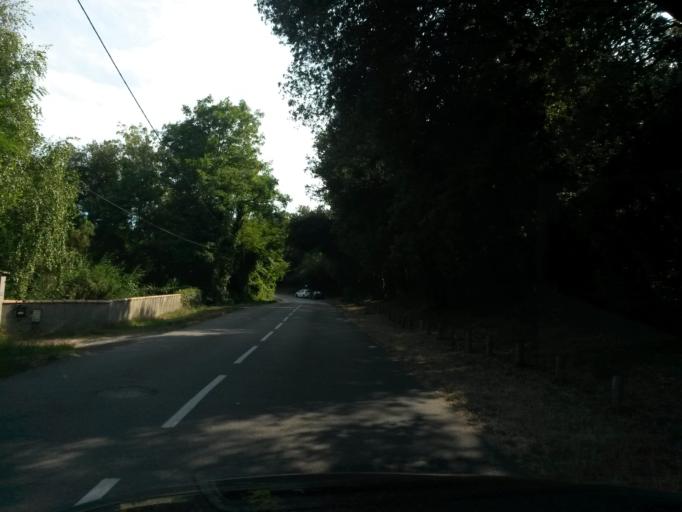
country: FR
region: Pays de la Loire
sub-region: Departement de la Vendee
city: Olonne-sur-Mer
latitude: 46.5415
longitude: -1.8126
